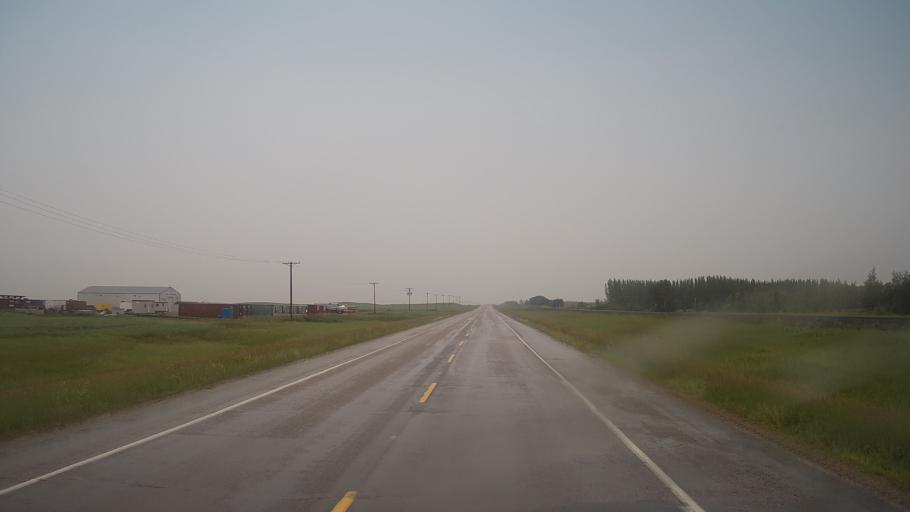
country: CA
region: Saskatchewan
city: Biggar
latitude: 52.0877
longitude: -108.0456
